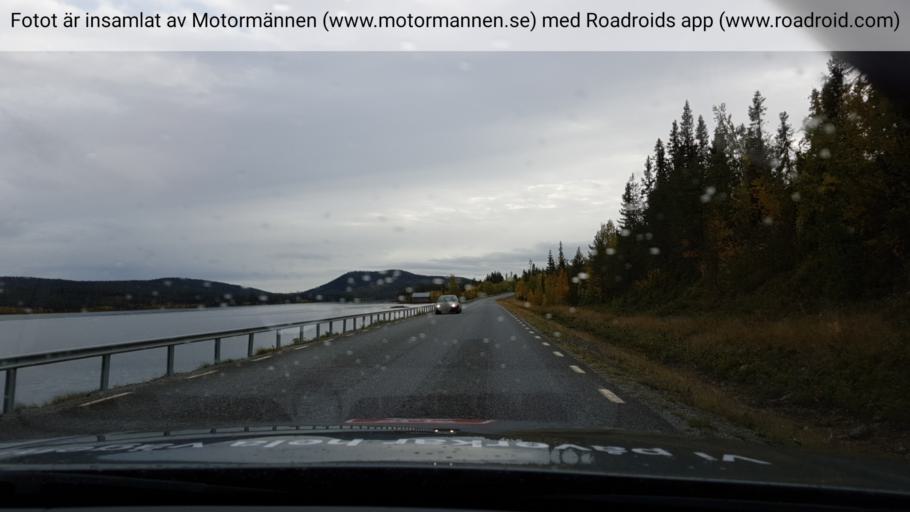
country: SE
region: Vaesterbotten
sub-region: Vilhelmina Kommun
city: Sjoberg
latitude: 64.9250
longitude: 15.8657
